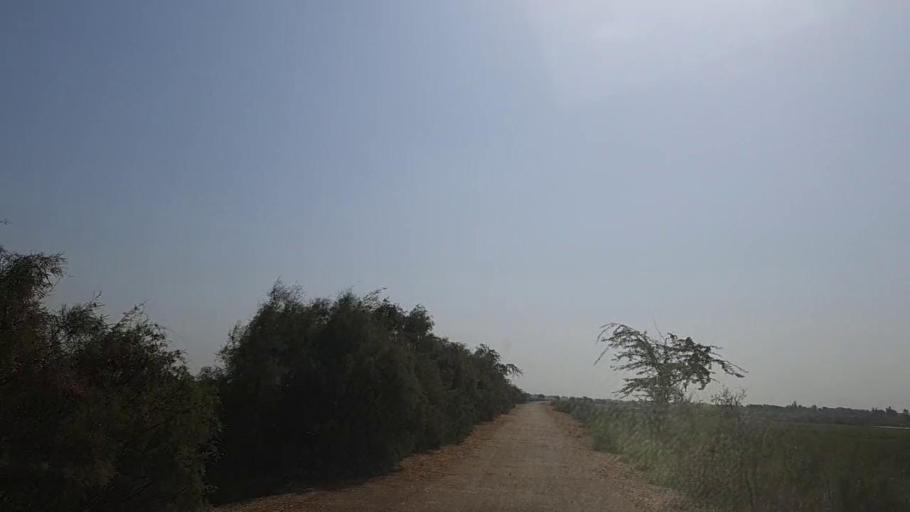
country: PK
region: Sindh
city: Daro Mehar
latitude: 24.7112
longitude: 68.1226
